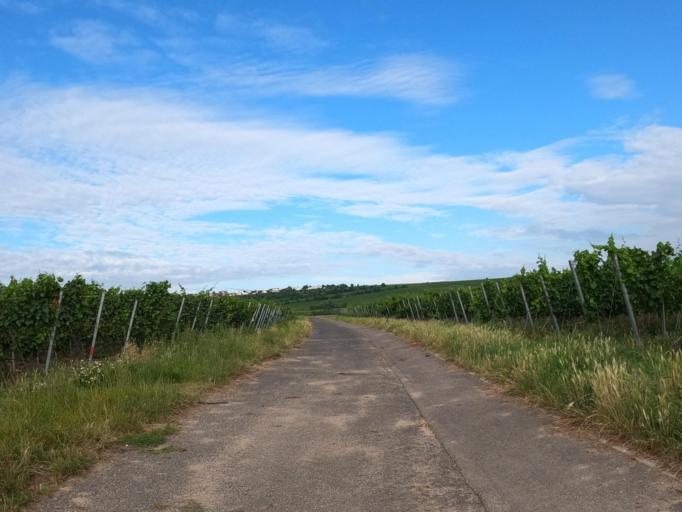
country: DE
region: Rheinland-Pfalz
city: Dackenheim
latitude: 49.5135
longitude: 8.1983
